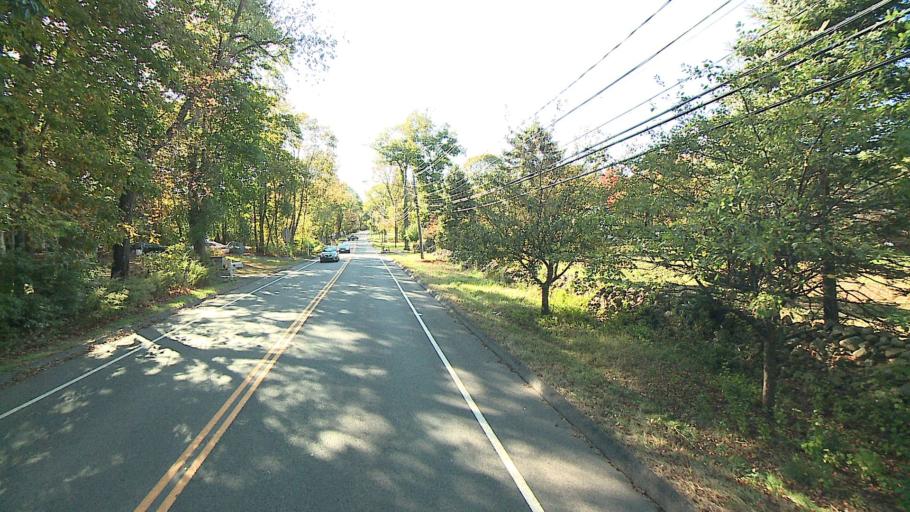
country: US
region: Connecticut
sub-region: Fairfield County
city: Westport
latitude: 41.1577
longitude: -73.3944
